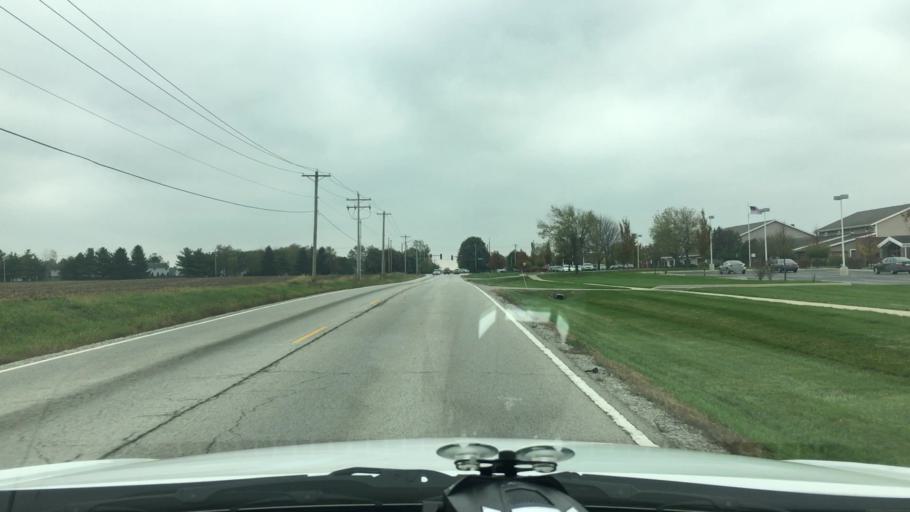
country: US
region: Illinois
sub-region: Champaign County
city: Champaign
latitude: 40.0987
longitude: -88.3183
